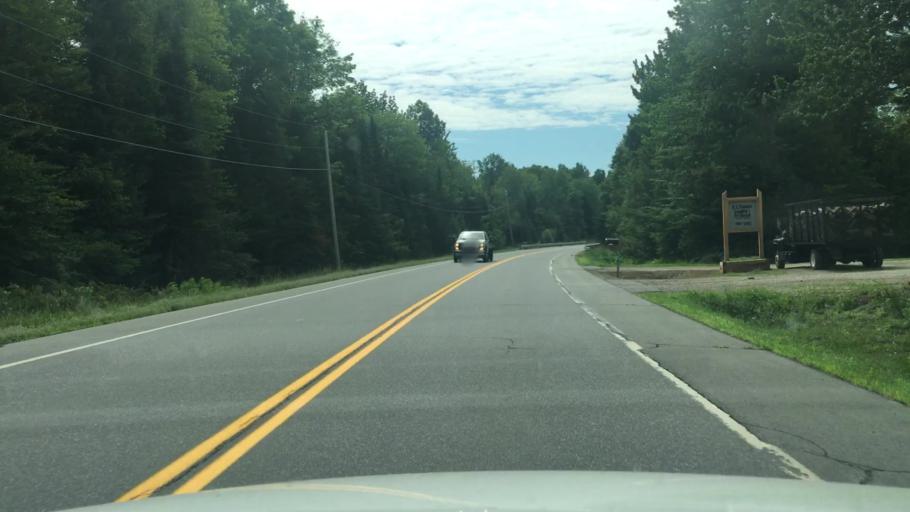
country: US
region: Maine
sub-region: Waldo County
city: Troy
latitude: 44.5994
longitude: -69.2875
